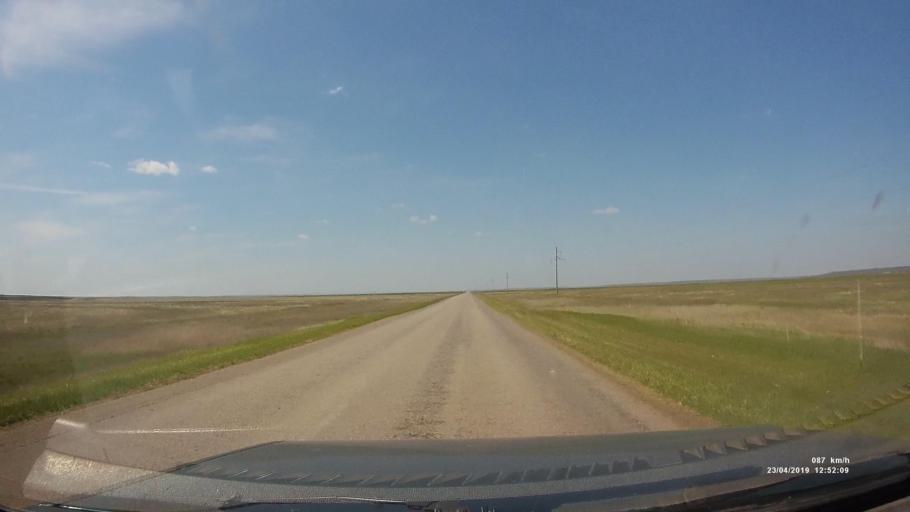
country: RU
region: Kalmykiya
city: Yashalta
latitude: 46.5619
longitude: 42.6132
